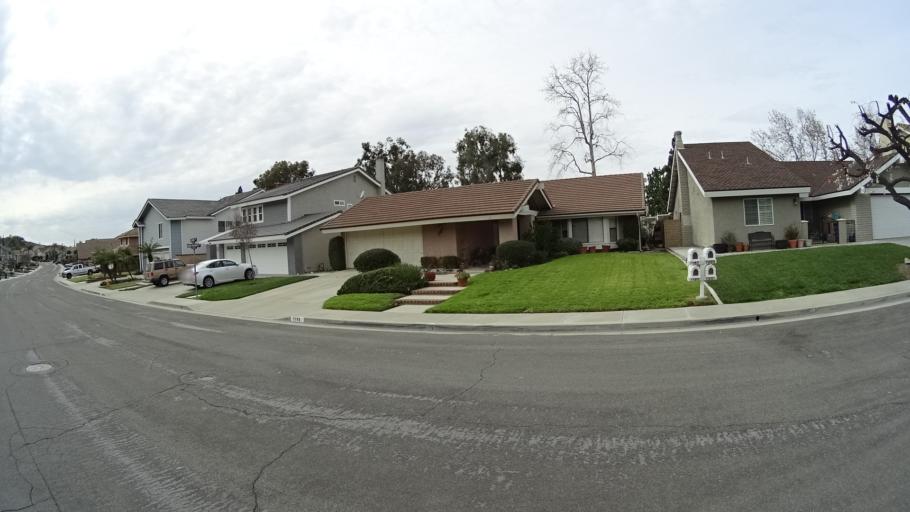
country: US
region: California
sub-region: Orange County
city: Villa Park
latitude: 33.8404
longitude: -117.7427
